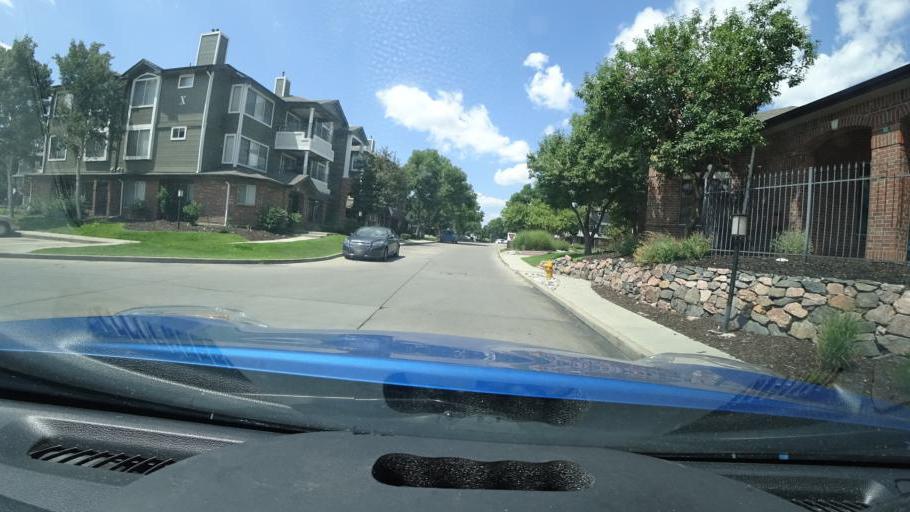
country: US
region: Colorado
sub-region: Adams County
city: Aurora
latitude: 39.6992
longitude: -104.8774
